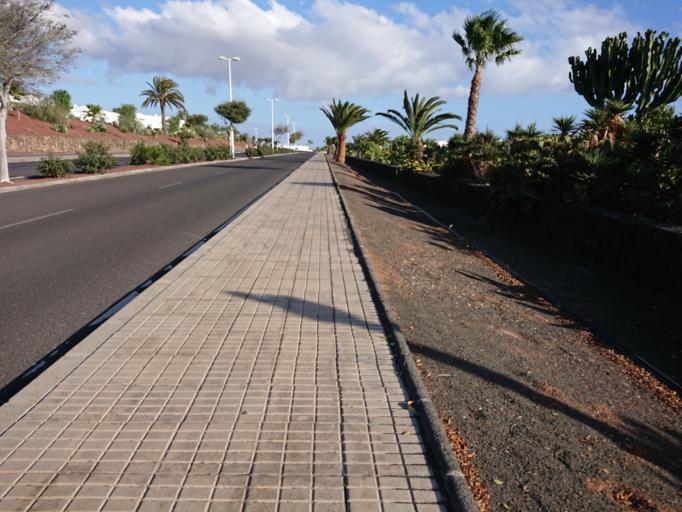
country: ES
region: Canary Islands
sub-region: Provincia de Las Palmas
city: Playa Blanca
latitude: 28.8653
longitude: -13.8477
